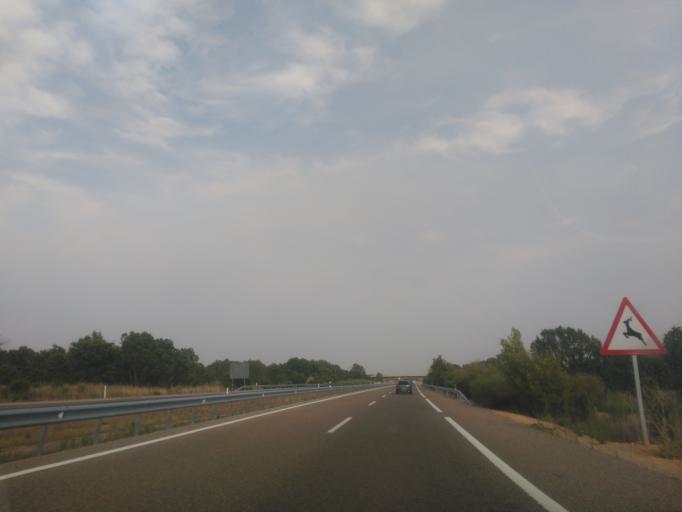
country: ES
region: Castille and Leon
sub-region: Provincia de Zamora
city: Mombuey
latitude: 42.0173
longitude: -6.3169
